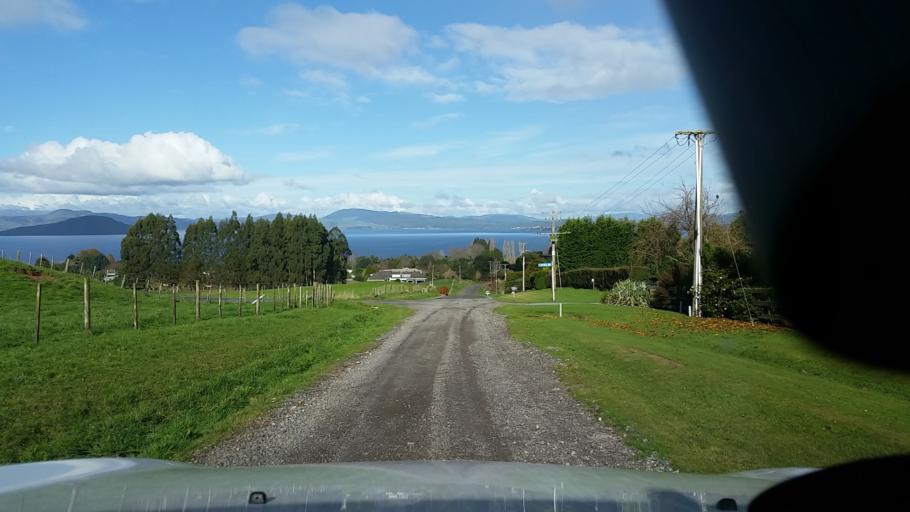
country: NZ
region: Bay of Plenty
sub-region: Rotorua District
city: Rotorua
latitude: -38.0307
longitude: 176.2259
